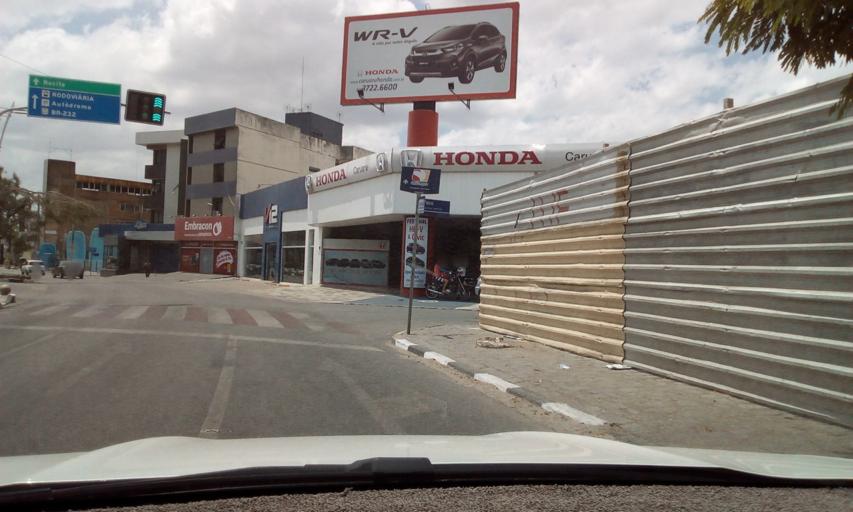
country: BR
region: Pernambuco
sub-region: Caruaru
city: Caruaru
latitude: -8.2682
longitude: -35.9765
